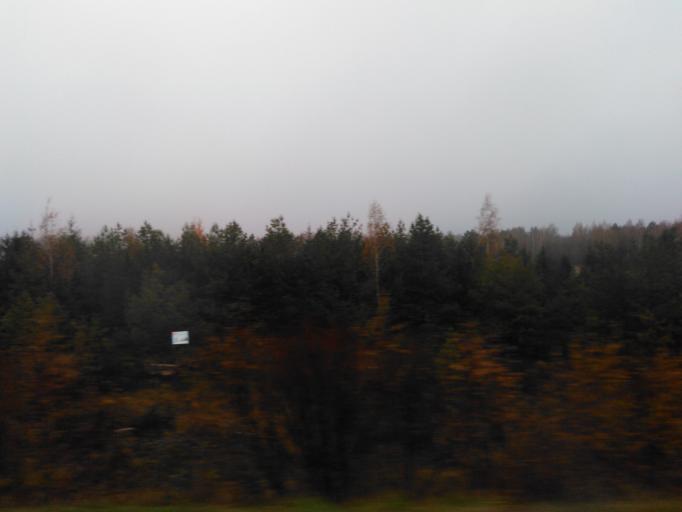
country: RU
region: Tatarstan
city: Sviyazhsk
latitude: 55.7291
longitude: 48.7653
